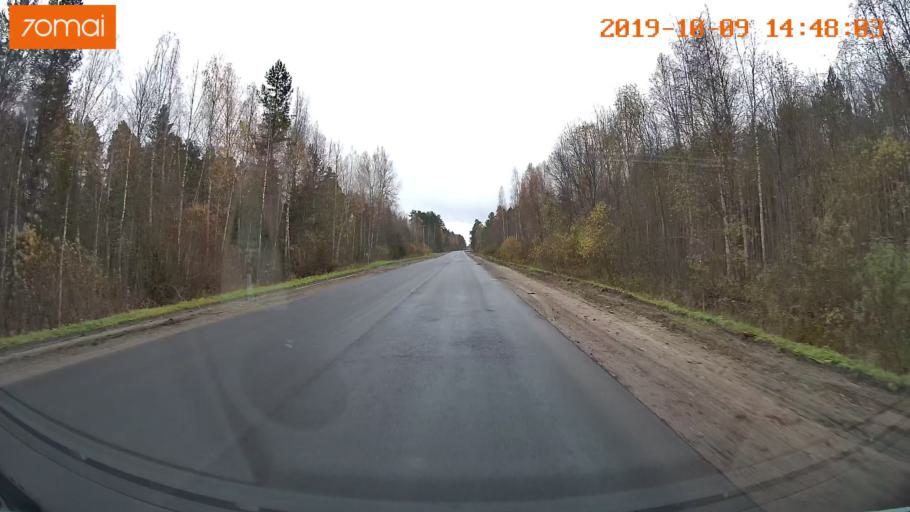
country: RU
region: Kostroma
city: Chistyye Bory
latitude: 58.4105
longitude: 41.5735
